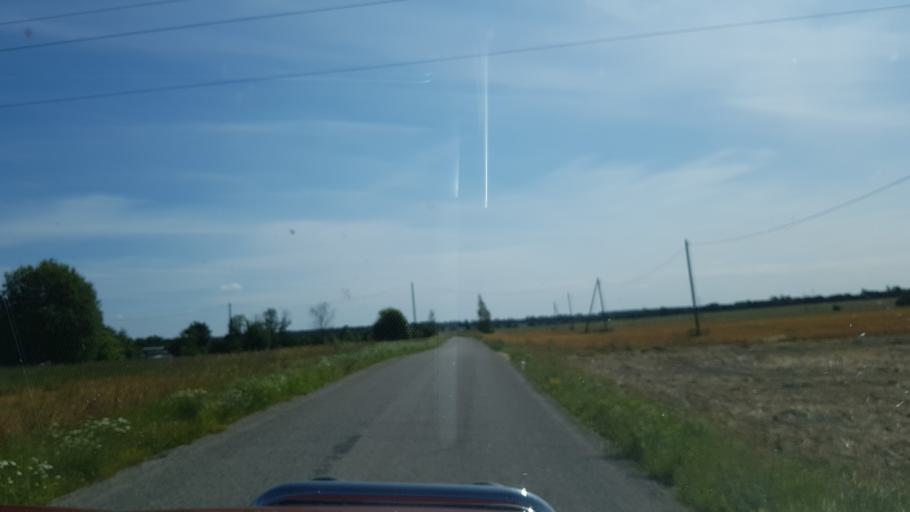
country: EE
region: Jaervamaa
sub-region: Jaerva-Jaani vald
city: Jarva-Jaani
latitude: 59.0883
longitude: 25.7344
